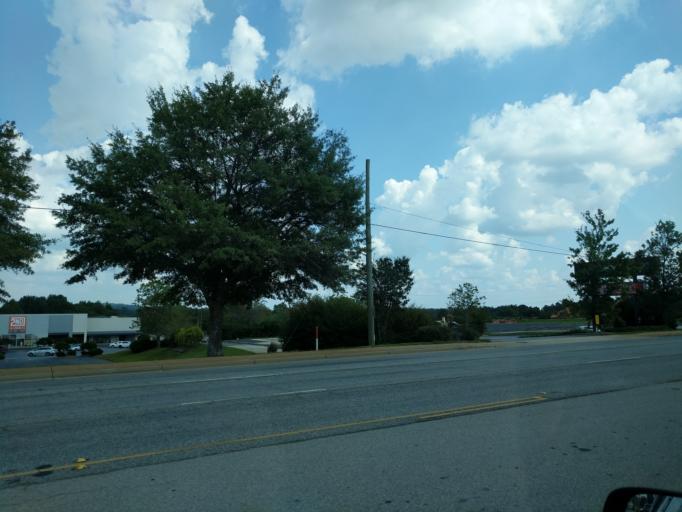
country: US
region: South Carolina
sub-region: Greenville County
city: Greenville
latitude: 34.8265
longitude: -82.3458
